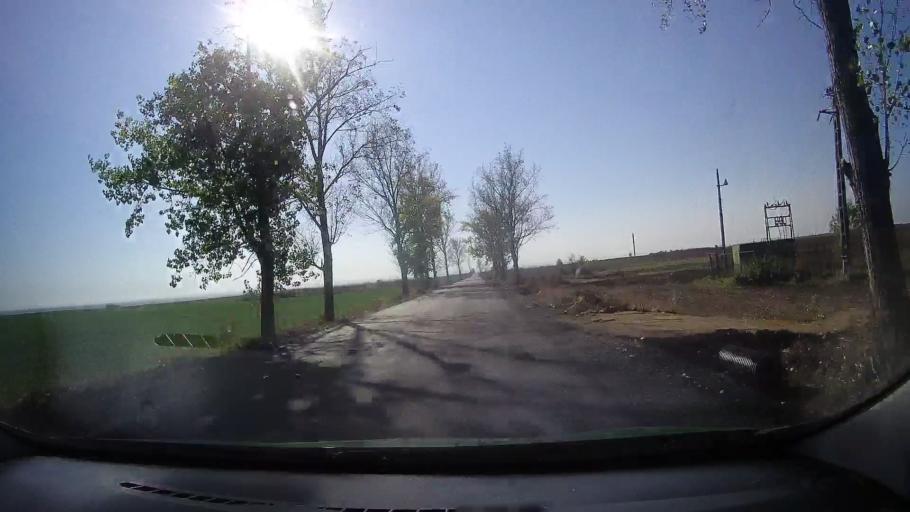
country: RO
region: Satu Mare
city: Carei
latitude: 47.6515
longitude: 22.4620
